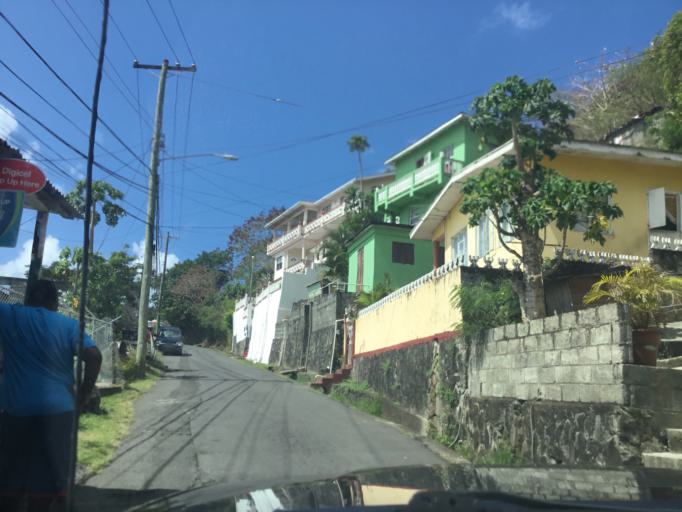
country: VC
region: Saint George
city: Kingstown Park
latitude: 13.1616
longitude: -61.2353
